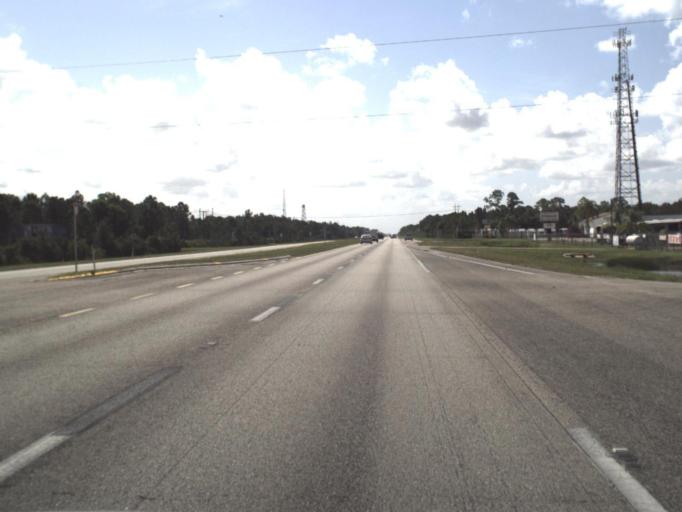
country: US
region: Florida
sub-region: Charlotte County
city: Charlotte Park
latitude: 26.8425
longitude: -81.9779
